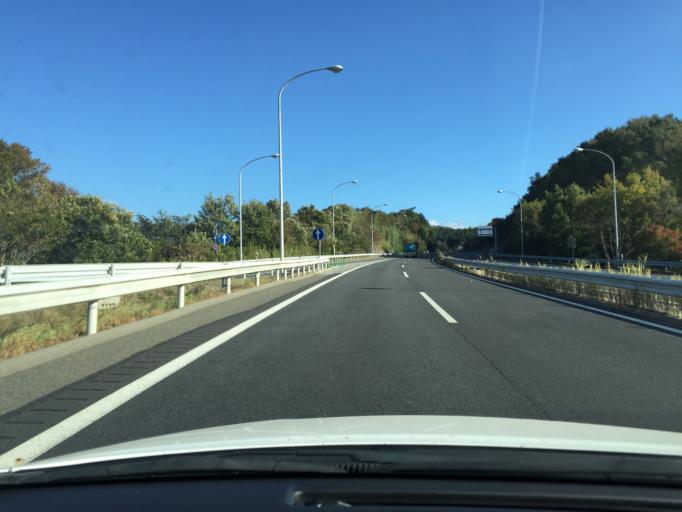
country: JP
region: Fukushima
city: Miharu
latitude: 37.4419
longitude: 140.4419
